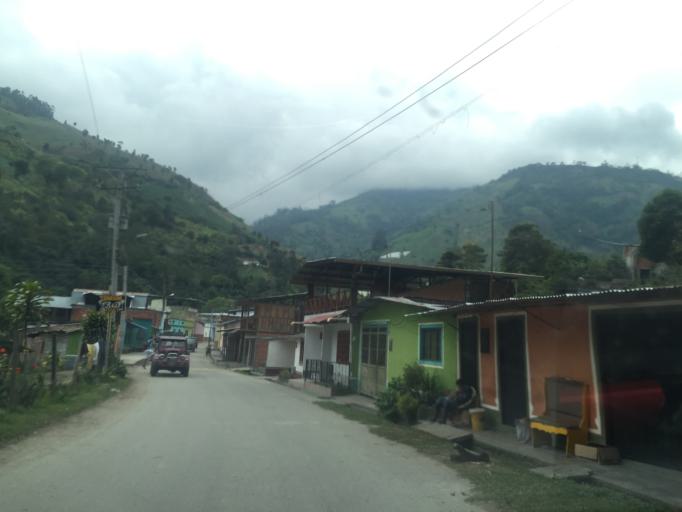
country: CO
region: Tolima
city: Cajamarca
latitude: 4.3990
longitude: -75.4443
